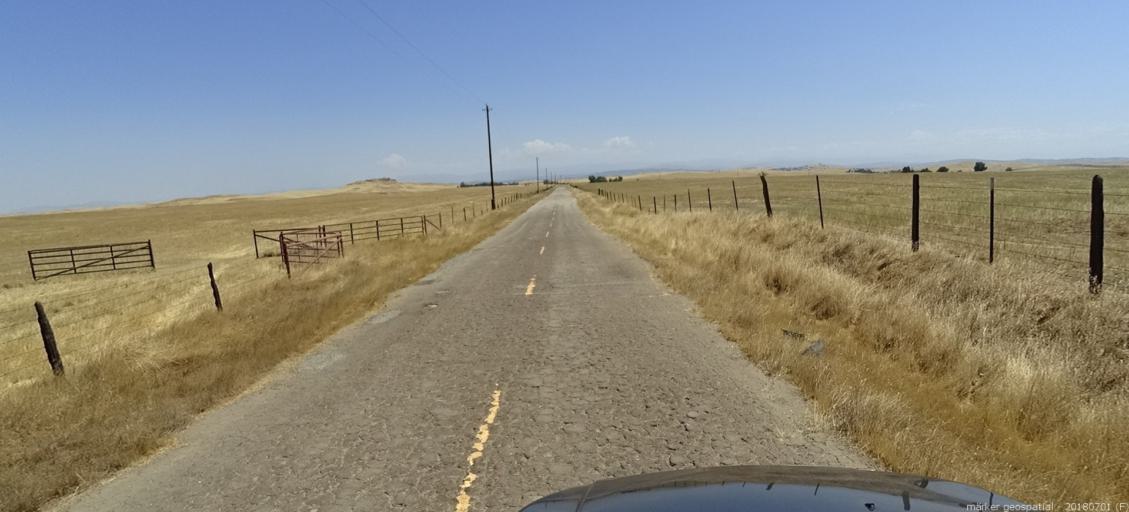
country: US
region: California
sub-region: Madera County
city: Madera Acres
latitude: 37.1043
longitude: -119.9969
